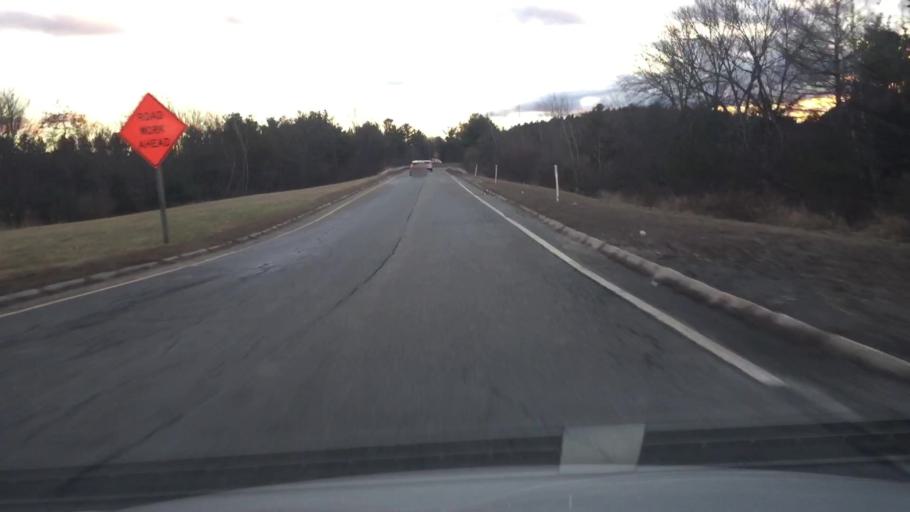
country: US
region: Massachusetts
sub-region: Worcester County
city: West Boylston
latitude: 42.4034
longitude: -71.7984
